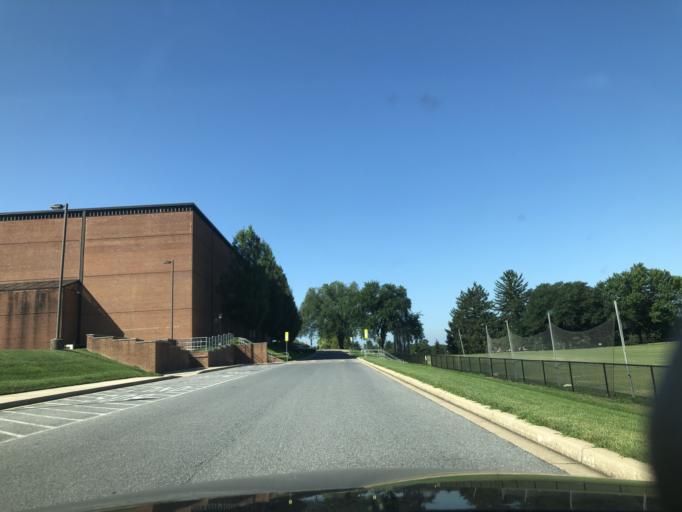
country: US
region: Maryland
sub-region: Carroll County
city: Westminster
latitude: 39.5871
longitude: -77.0006
